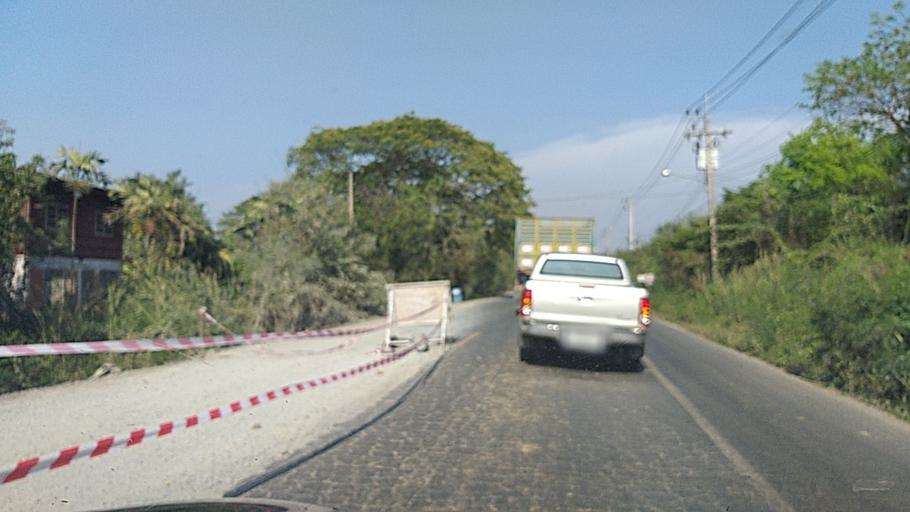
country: TH
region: Nonthaburi
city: Bang Yai
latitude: 13.8794
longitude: 100.3040
